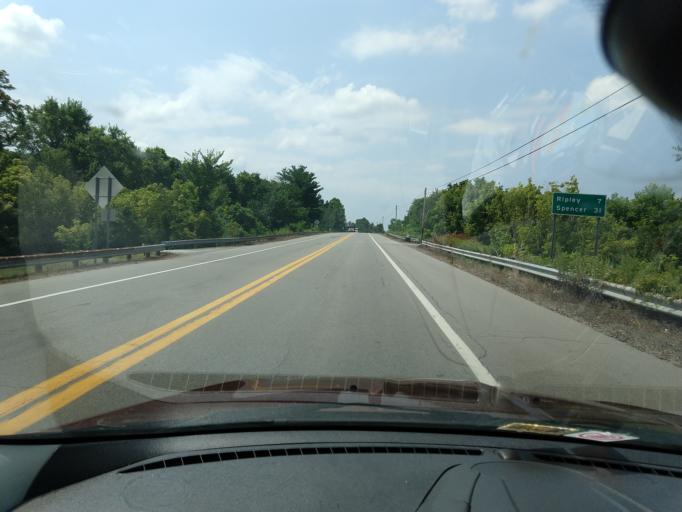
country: US
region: West Virginia
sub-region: Jackson County
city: Ravenswood
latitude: 38.8659
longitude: -81.8180
